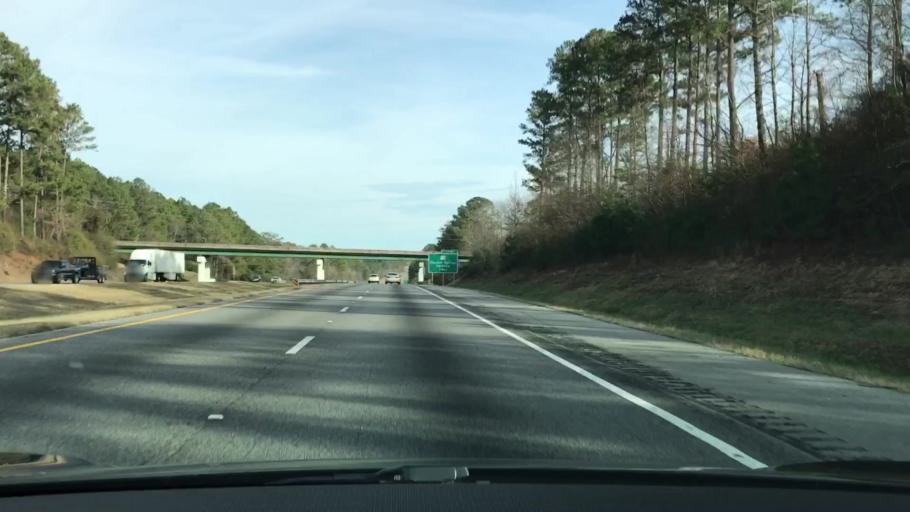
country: US
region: Georgia
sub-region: Walton County
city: Social Circle
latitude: 33.6114
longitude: -83.7221
